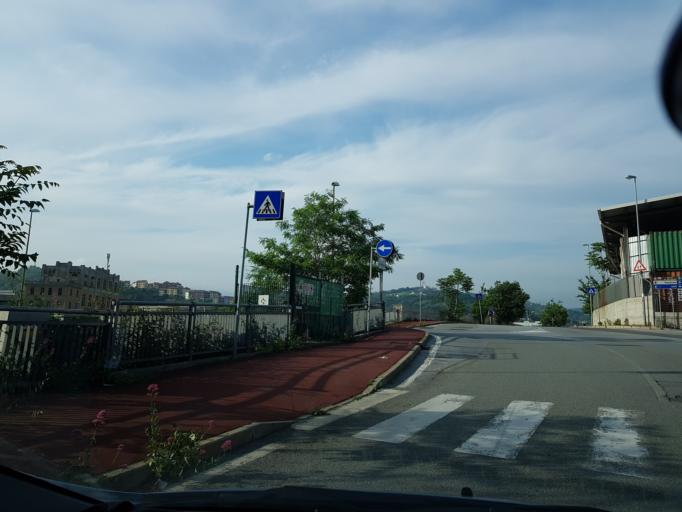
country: IT
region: Liguria
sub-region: Provincia di Genova
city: Manesseno
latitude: 44.4639
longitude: 8.8991
